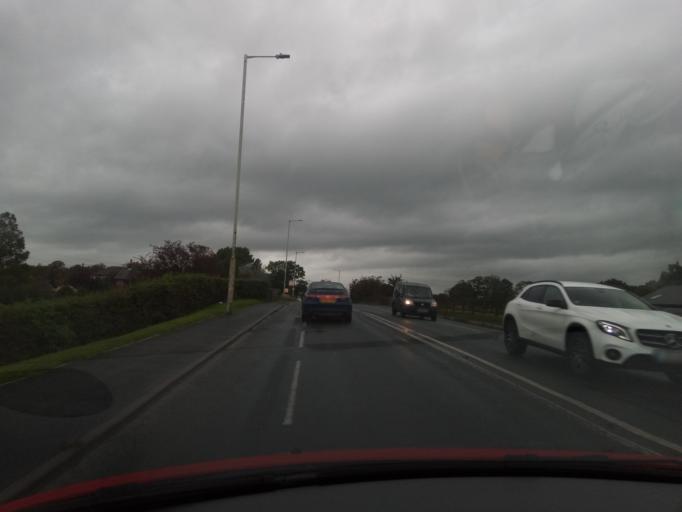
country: GB
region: England
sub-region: Lancashire
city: Catterall
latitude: 53.8627
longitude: -2.7454
